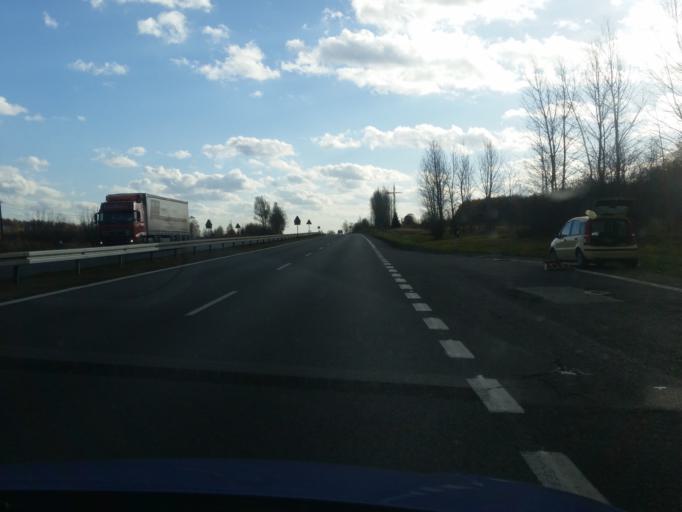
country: PL
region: Silesian Voivodeship
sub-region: Powiat czestochowski
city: Kamienica Polska
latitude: 50.6404
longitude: 19.1358
